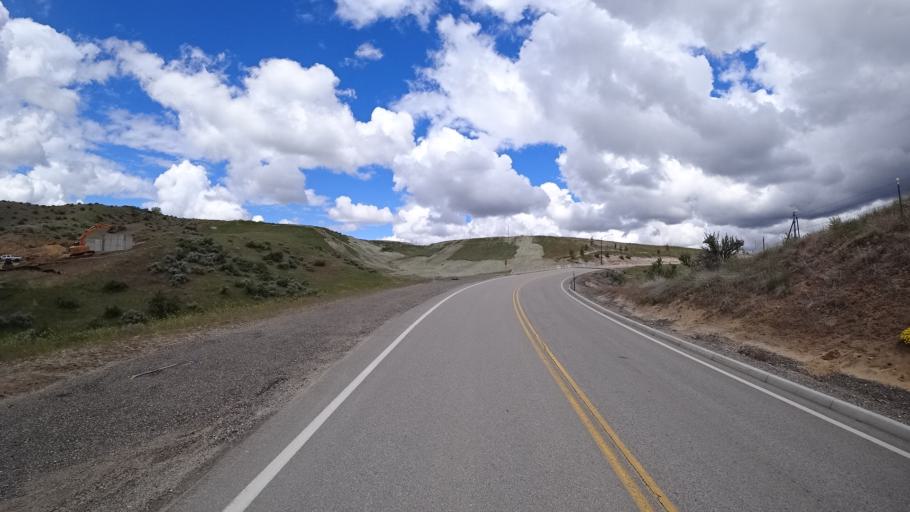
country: US
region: Idaho
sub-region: Ada County
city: Boise
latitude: 43.6626
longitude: -116.1915
